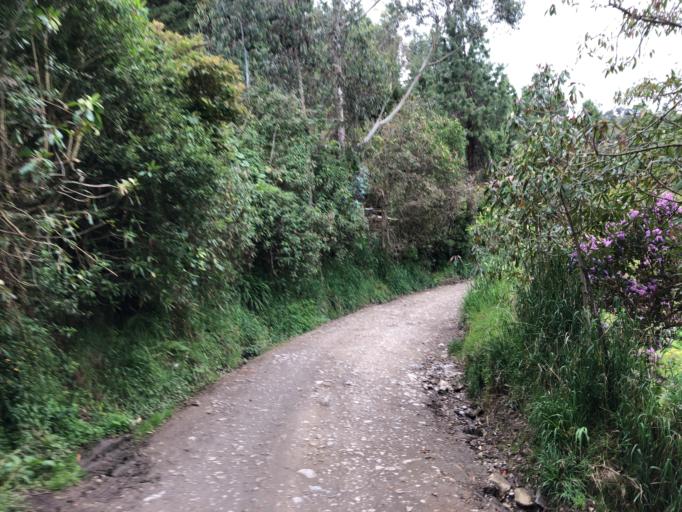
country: CO
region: Cauca
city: Totoro
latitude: 2.5050
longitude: -76.3600
